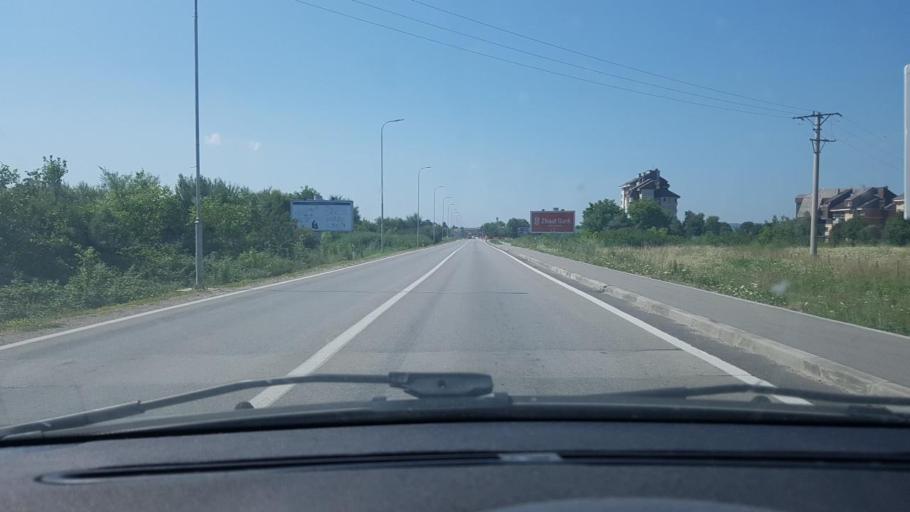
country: BA
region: Federation of Bosnia and Herzegovina
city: Bihac
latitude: 44.8091
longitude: 15.8842
